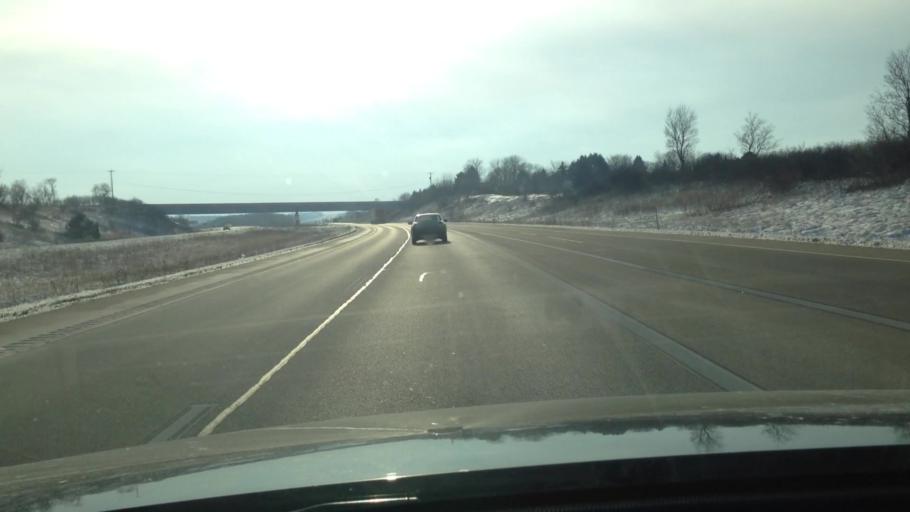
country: US
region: Wisconsin
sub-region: Walworth County
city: East Troy
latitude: 42.7451
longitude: -88.4498
